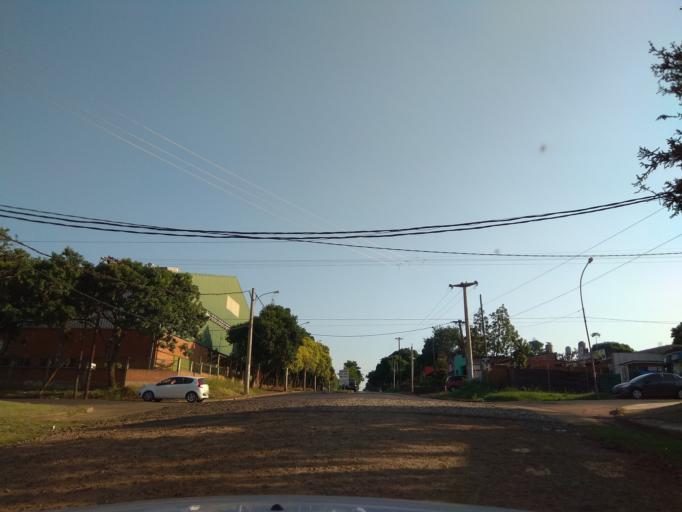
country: AR
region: Misiones
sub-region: Departamento de Capital
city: Posadas
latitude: -27.3641
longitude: -55.9275
